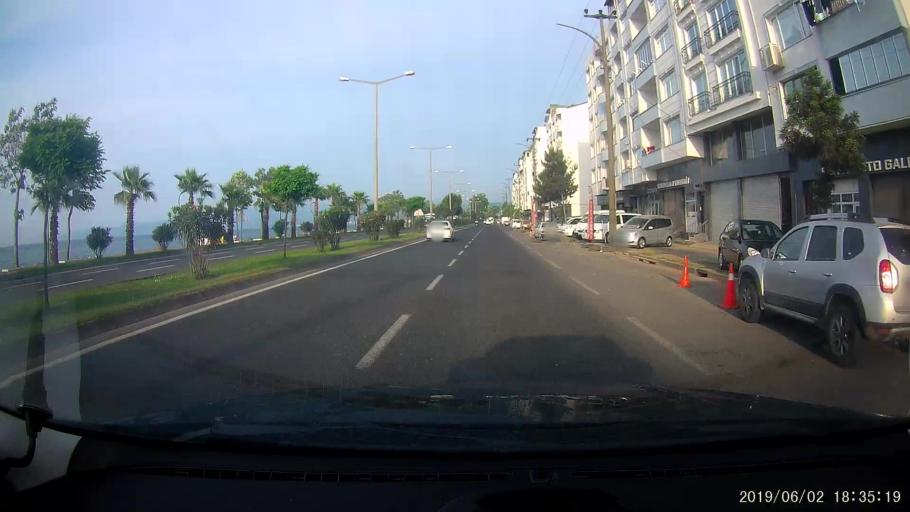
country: TR
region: Ordu
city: Fatsa
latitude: 41.0268
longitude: 37.5138
